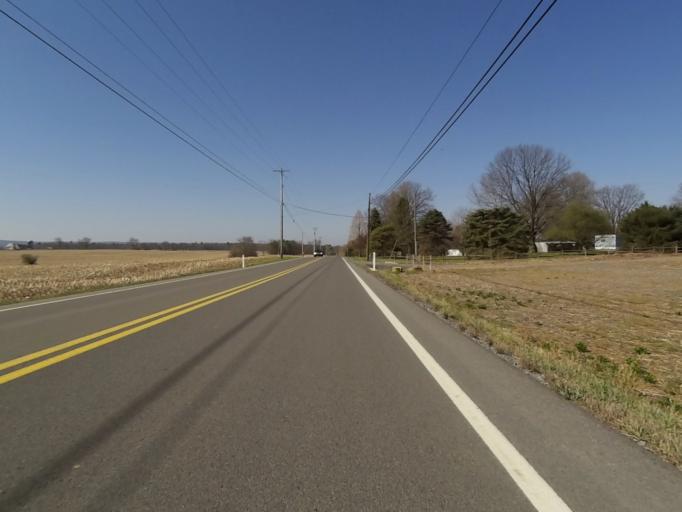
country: US
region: Pennsylvania
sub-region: Centre County
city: Park Forest Village
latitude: 40.7733
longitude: -77.9066
